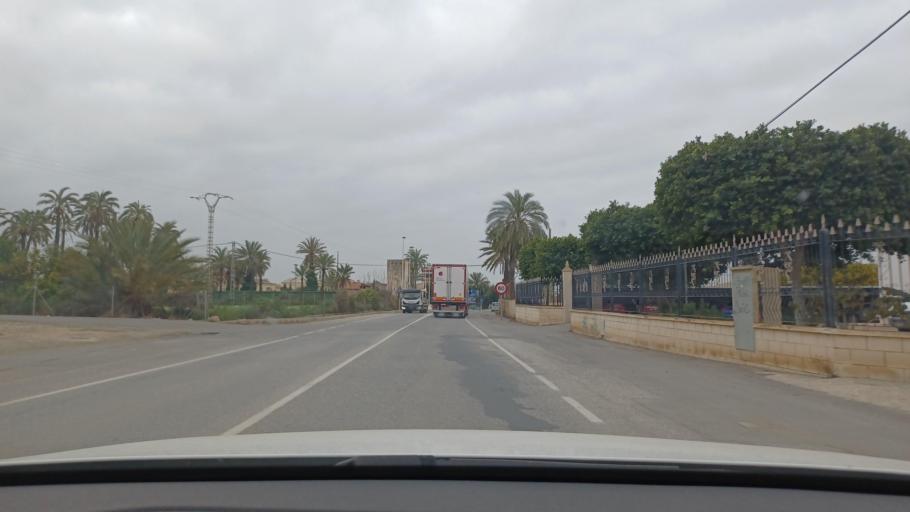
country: ES
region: Valencia
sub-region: Provincia de Alicante
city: Elche
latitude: 38.2486
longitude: -0.7048
